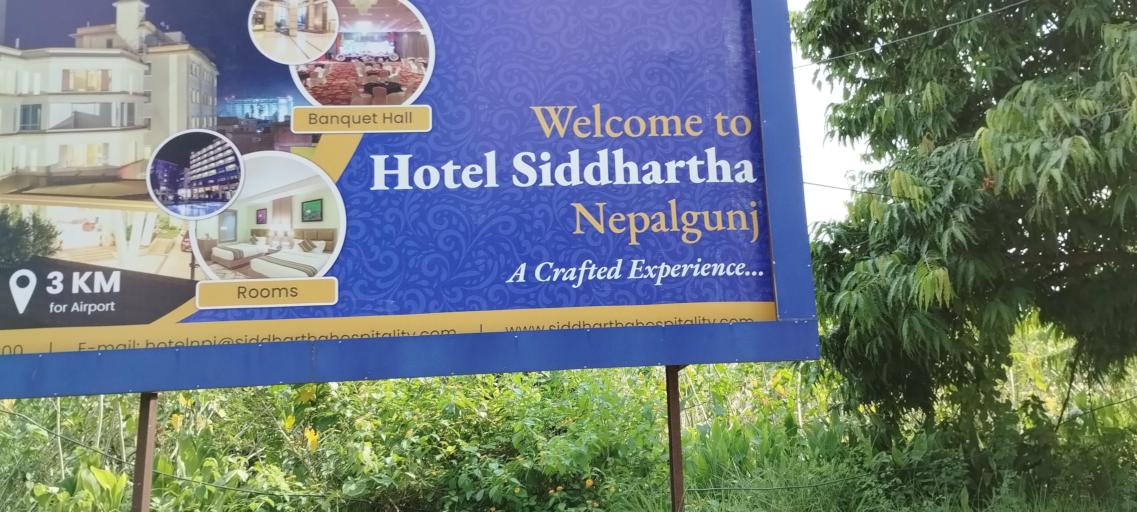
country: NP
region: Mid Western
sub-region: Bheri Zone
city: Nepalgunj
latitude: 28.1002
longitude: 81.6672
